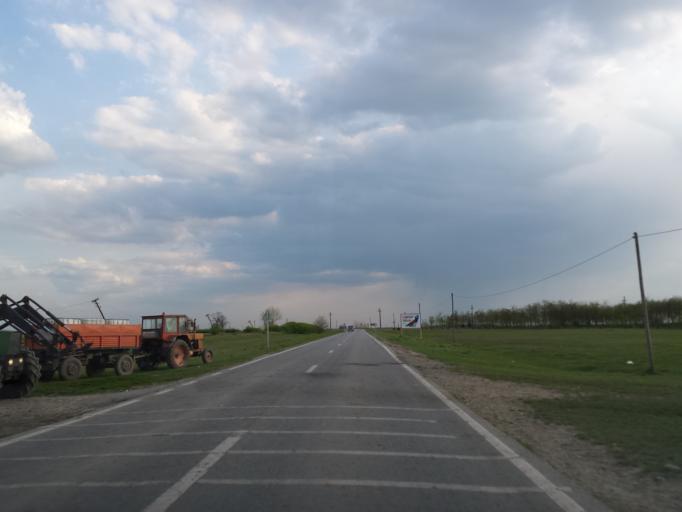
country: RO
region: Timis
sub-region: Comuna Cenad
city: Cenad
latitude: 46.1154
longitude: 20.5958
